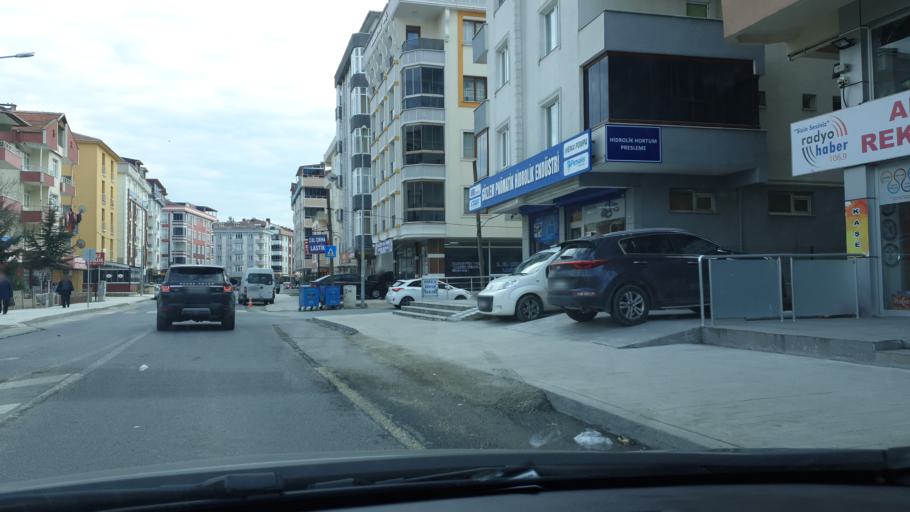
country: TR
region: Tekirdag
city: Cerkezkoey
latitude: 41.2875
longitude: 27.9923
